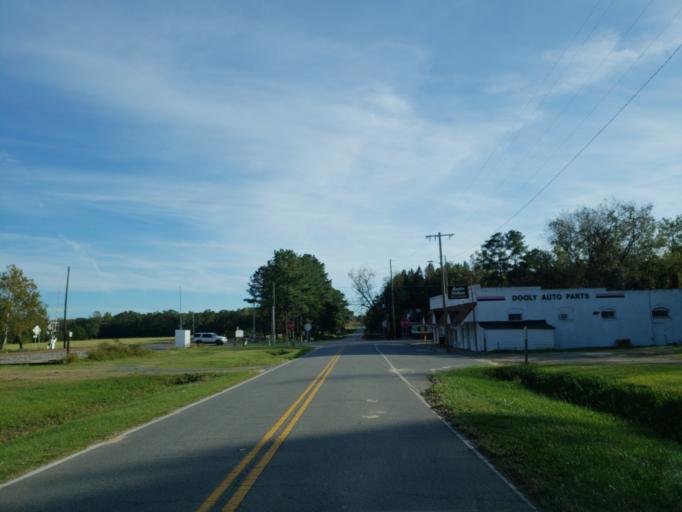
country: US
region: Georgia
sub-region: Dooly County
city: Vienna
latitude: 32.0913
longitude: -83.7876
